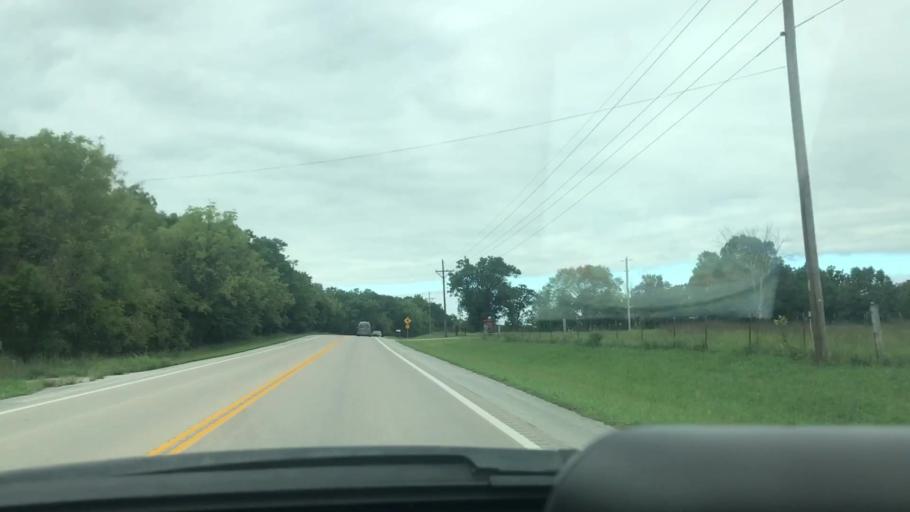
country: US
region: Missouri
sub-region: Hickory County
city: Hermitage
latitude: 37.8694
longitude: -93.1802
